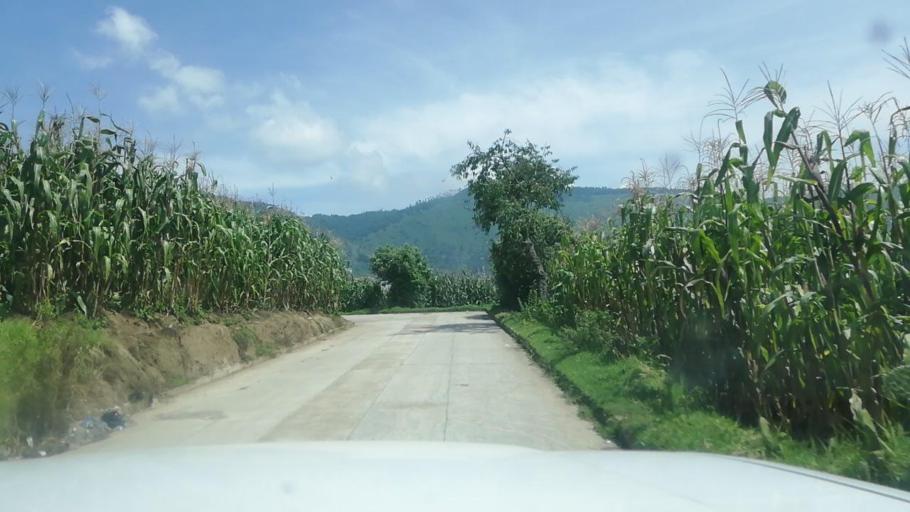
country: GT
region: Totonicapan
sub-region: Municipio de San Andres Xecul
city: San Andres Xecul
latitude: 14.8935
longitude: -91.4751
